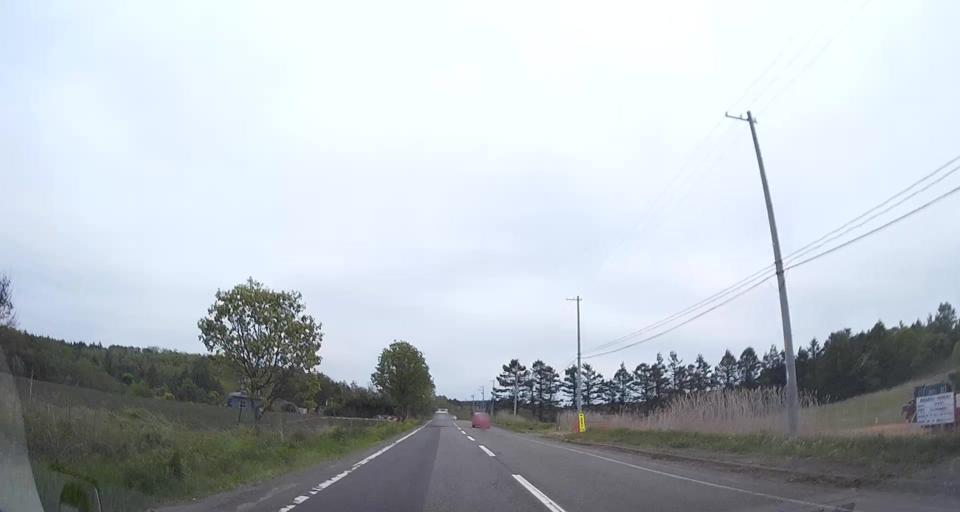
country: JP
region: Hokkaido
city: Chitose
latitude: 42.7730
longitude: 141.8356
